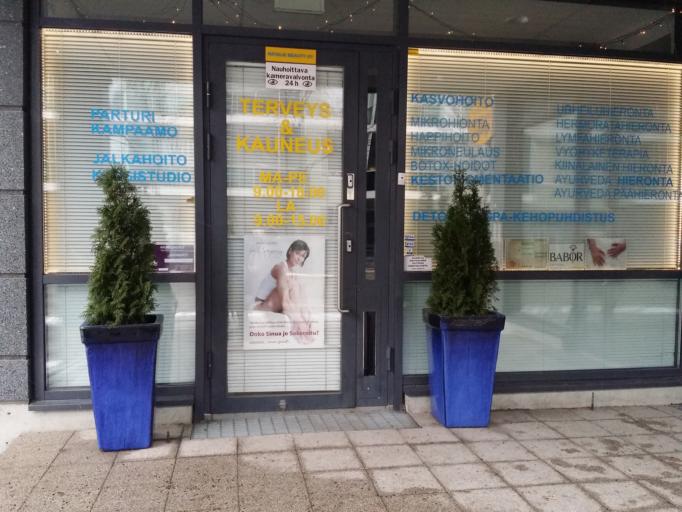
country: FI
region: Uusimaa
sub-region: Helsinki
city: Helsinki
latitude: 60.1867
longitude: 25.0310
